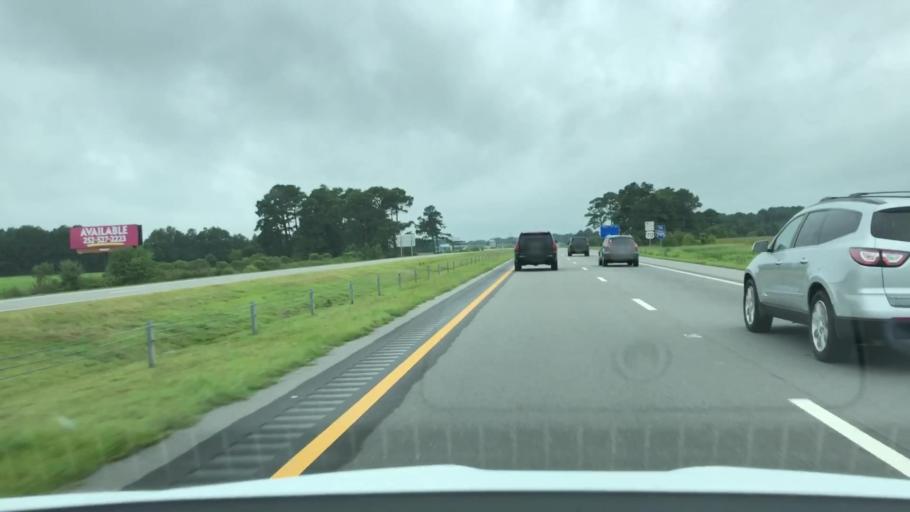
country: US
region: North Carolina
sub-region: Wayne County
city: Elroy
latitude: 35.4154
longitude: -77.9061
